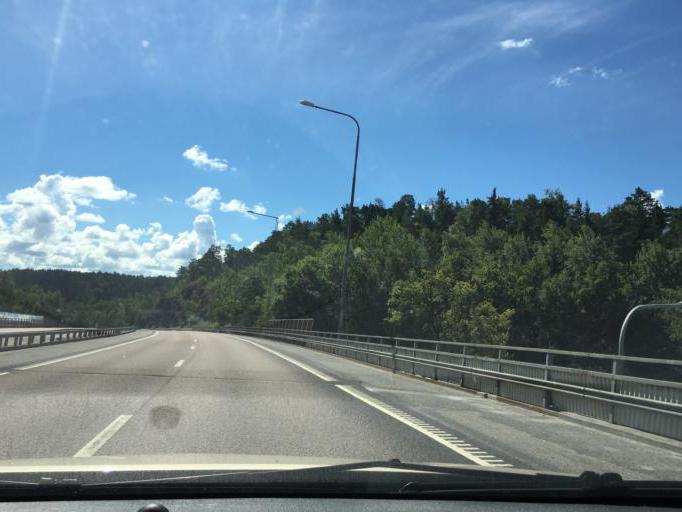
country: SE
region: Stockholm
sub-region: Nacka Kommun
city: Nacka
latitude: 59.3048
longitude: 18.1820
